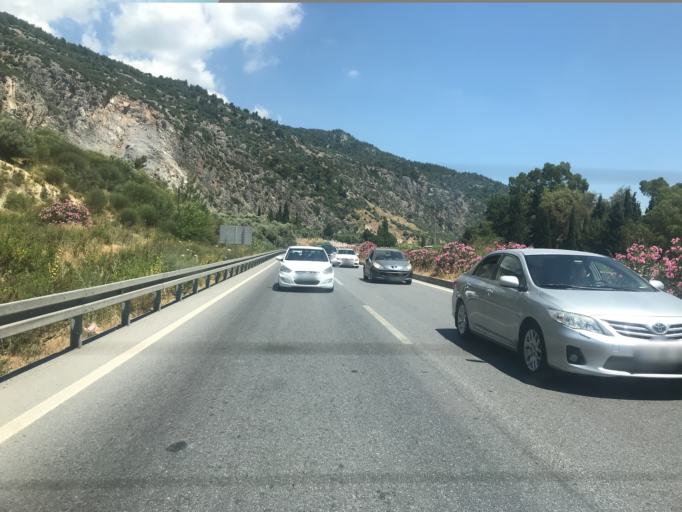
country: TR
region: Aydin
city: Soeke
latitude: 37.7914
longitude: 27.4663
